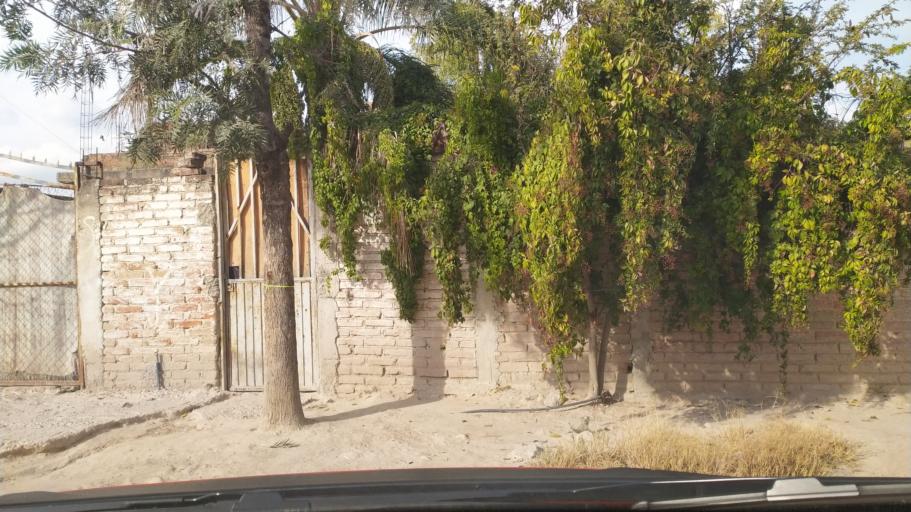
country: MX
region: Guanajuato
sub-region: San Francisco del Rincon
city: Fraccionamiento la Mezquitera
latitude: 21.0052
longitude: -101.8460
